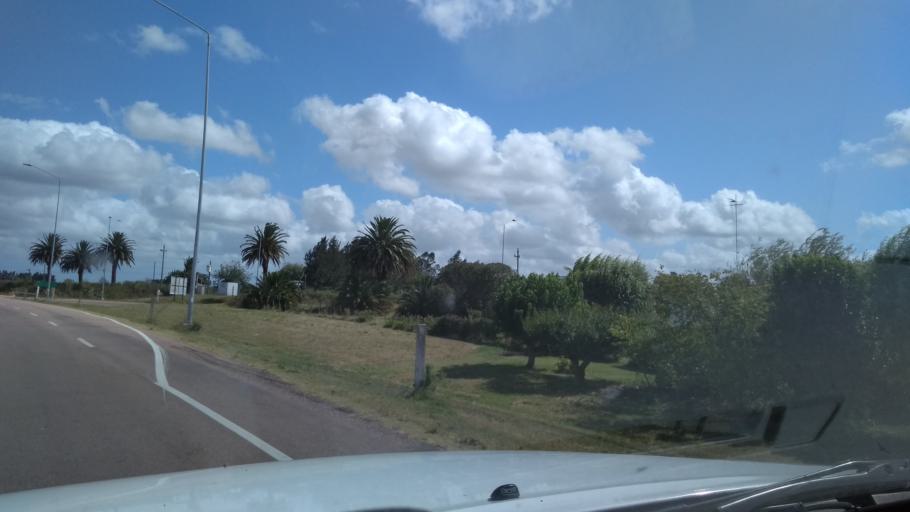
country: UY
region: Canelones
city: Sauce
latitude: -34.6635
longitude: -56.0577
